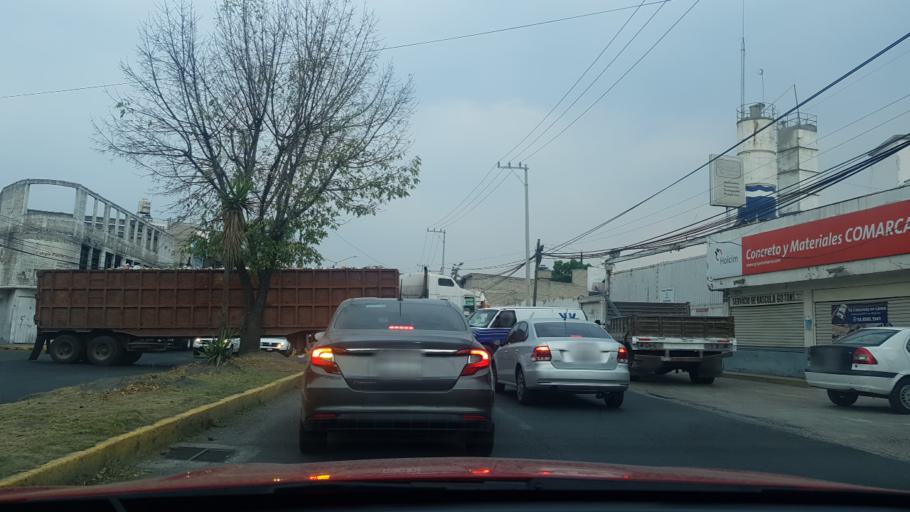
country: MX
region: Mexico
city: Cuautitlan Izcalli
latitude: 19.6044
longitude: -99.2242
